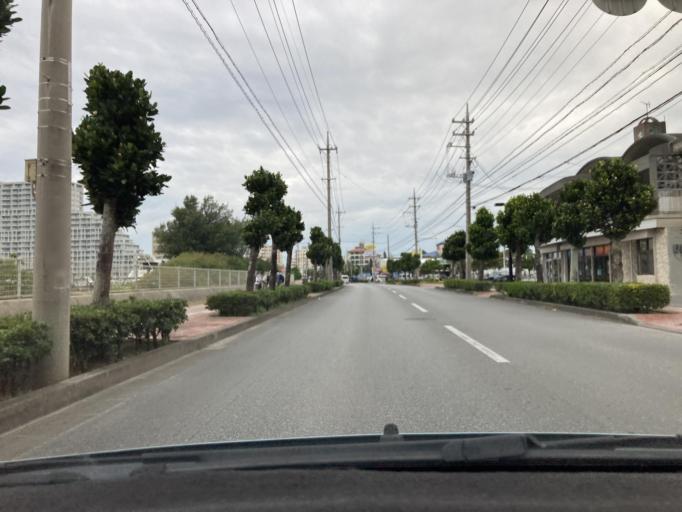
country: JP
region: Okinawa
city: Chatan
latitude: 26.3229
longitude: 127.7558
